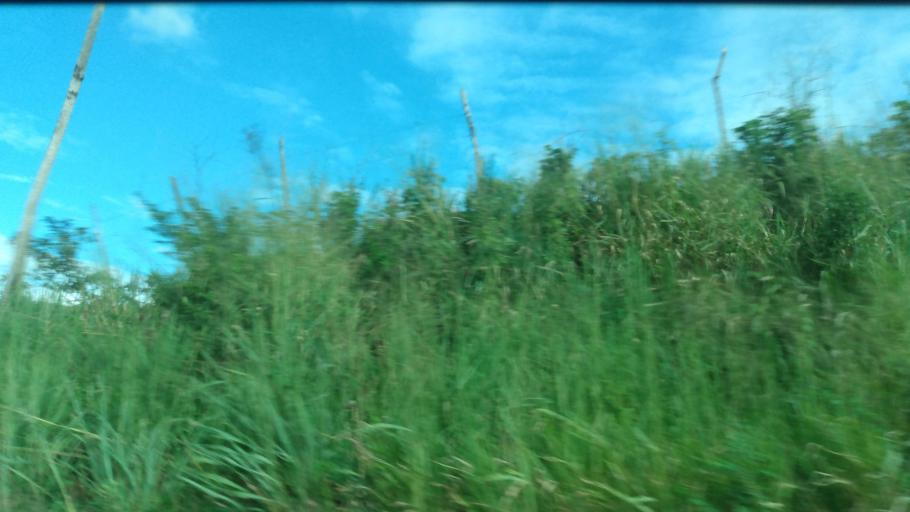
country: BR
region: Pernambuco
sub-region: Palmares
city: Palmares
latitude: -8.6937
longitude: -35.6432
